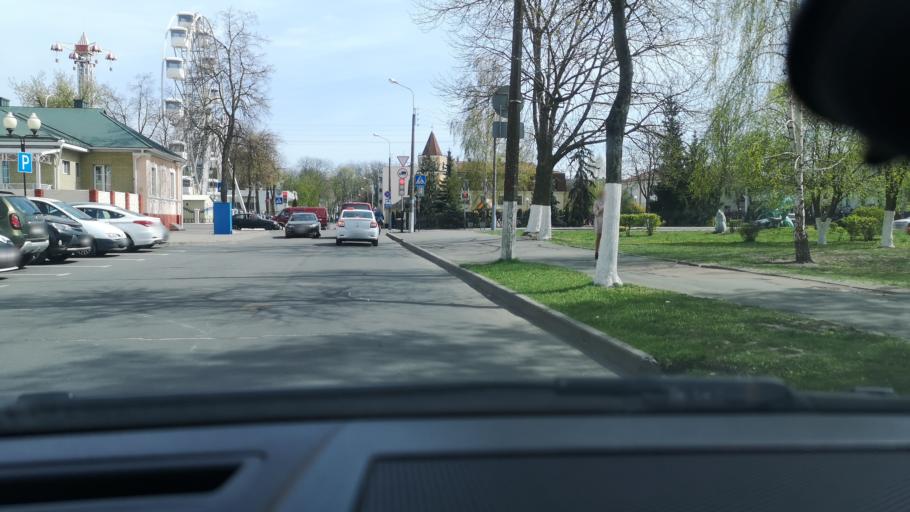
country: BY
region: Gomel
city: Gomel
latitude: 52.4198
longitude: 31.0091
